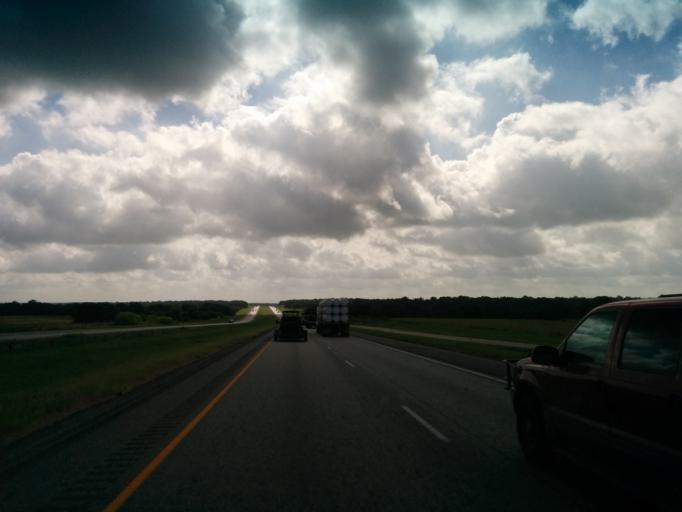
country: US
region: Texas
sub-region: Gonzales County
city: Waelder
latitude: 29.6586
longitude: -97.4114
